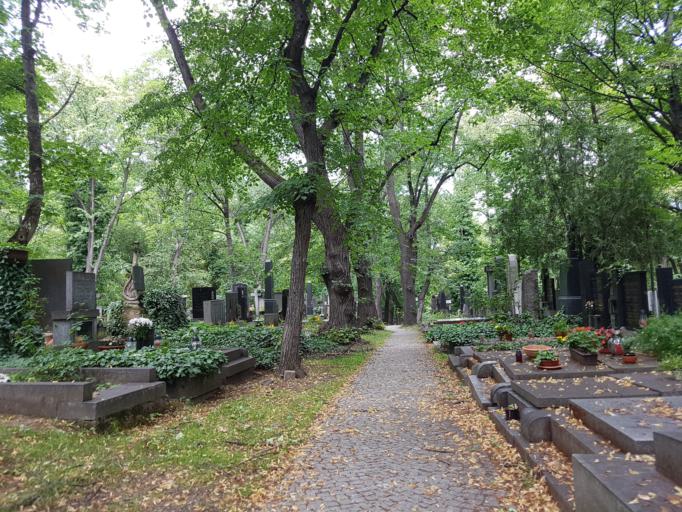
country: CZ
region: Praha
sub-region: Praha 8
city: Karlin
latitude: 50.0796
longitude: 14.4662
